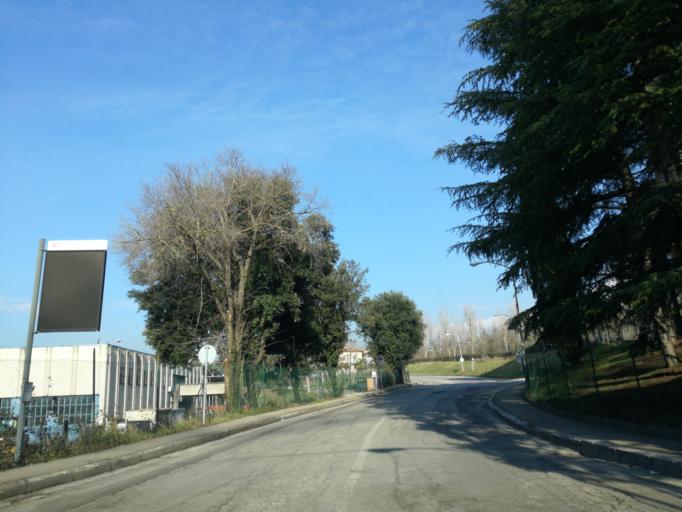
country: IT
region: Umbria
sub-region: Provincia di Perugia
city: Perugia
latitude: 43.1095
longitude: 12.3662
